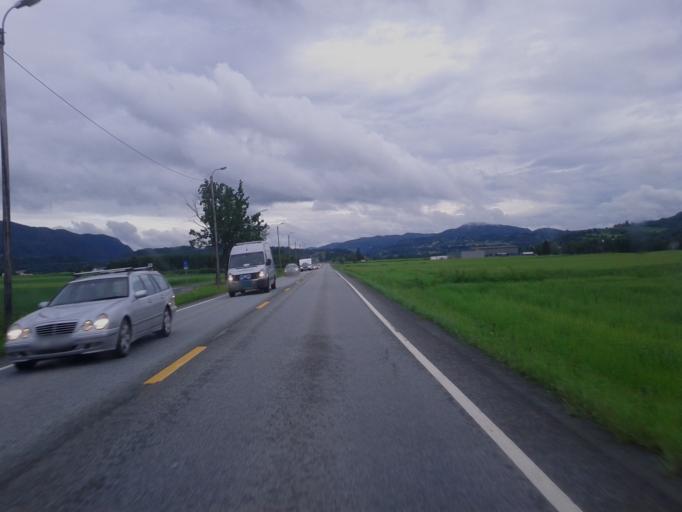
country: NO
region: Sor-Trondelag
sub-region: Melhus
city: Melhus
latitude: 63.3146
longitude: 10.2949
